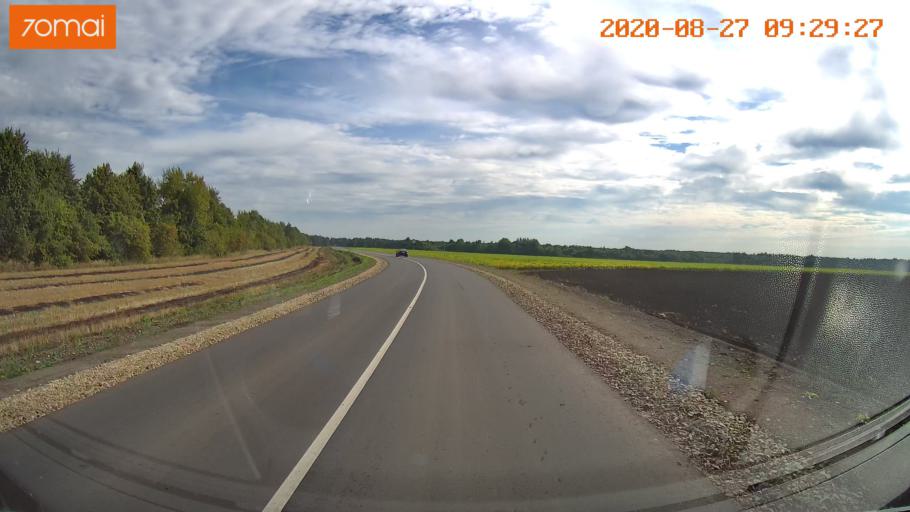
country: RU
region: Tula
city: Kazachka
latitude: 53.3144
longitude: 38.2228
